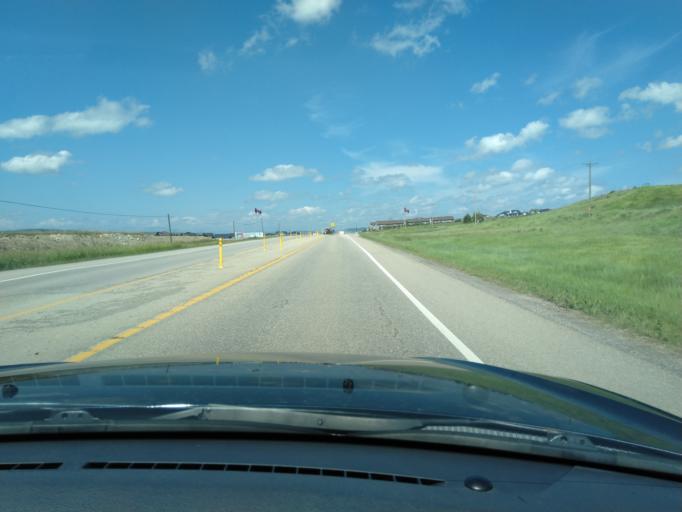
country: CA
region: Alberta
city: Cochrane
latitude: 51.2019
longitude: -114.4977
